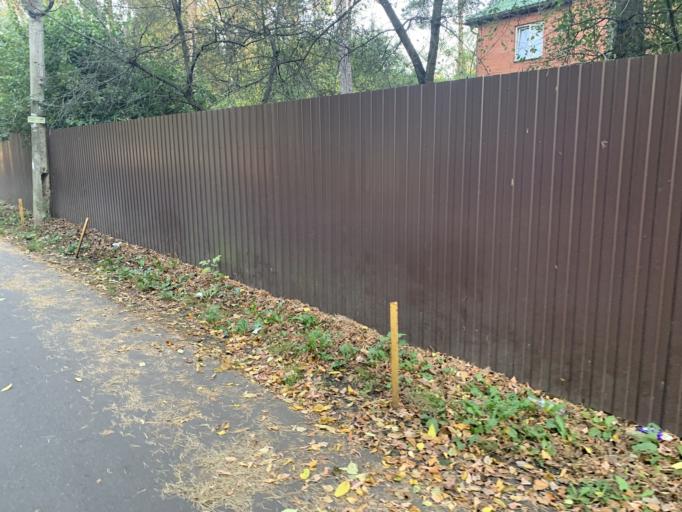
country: RU
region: Moskovskaya
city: Korolev
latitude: 55.9303
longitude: 37.7909
